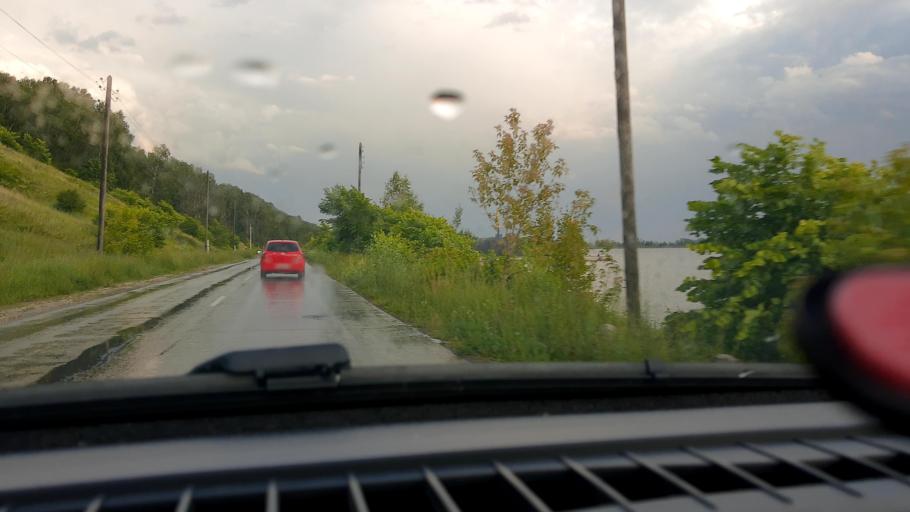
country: RU
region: Nizjnij Novgorod
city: Gorodets
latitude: 56.6780
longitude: 43.4401
